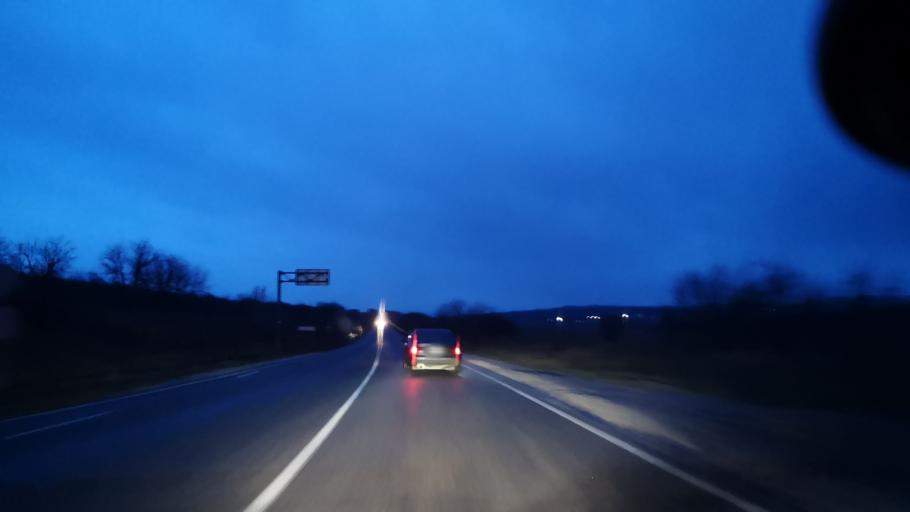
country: MD
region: Orhei
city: Orhei
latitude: 47.4053
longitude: 28.8172
